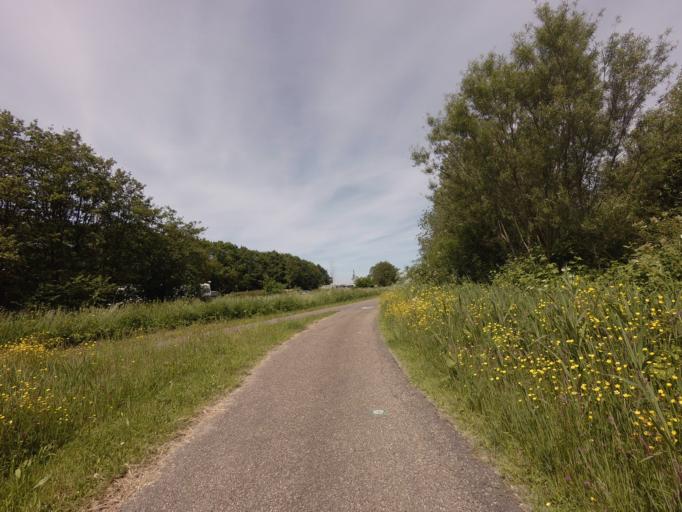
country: NL
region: North Holland
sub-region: Gemeente Zaanstad
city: Zaandam
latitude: 52.3876
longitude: 4.7775
